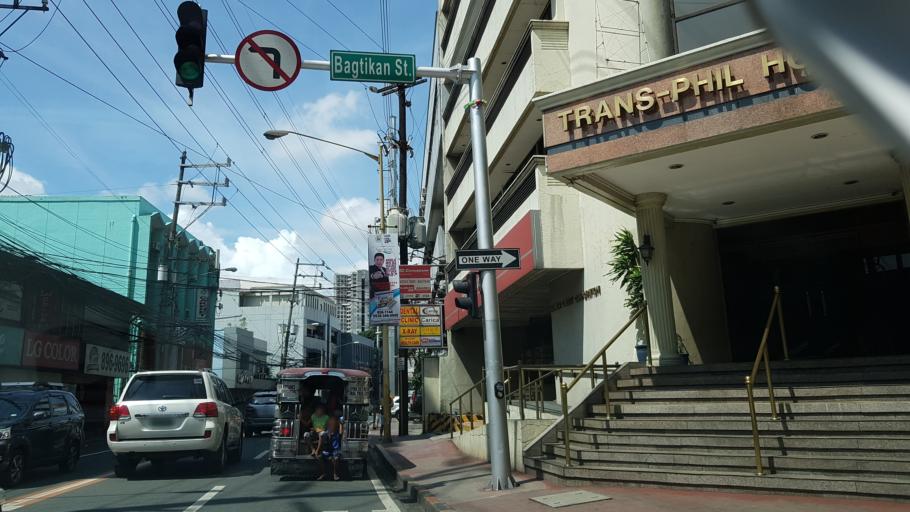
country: PH
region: Metro Manila
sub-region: Makati City
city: Makati City
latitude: 14.5623
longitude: 121.0108
